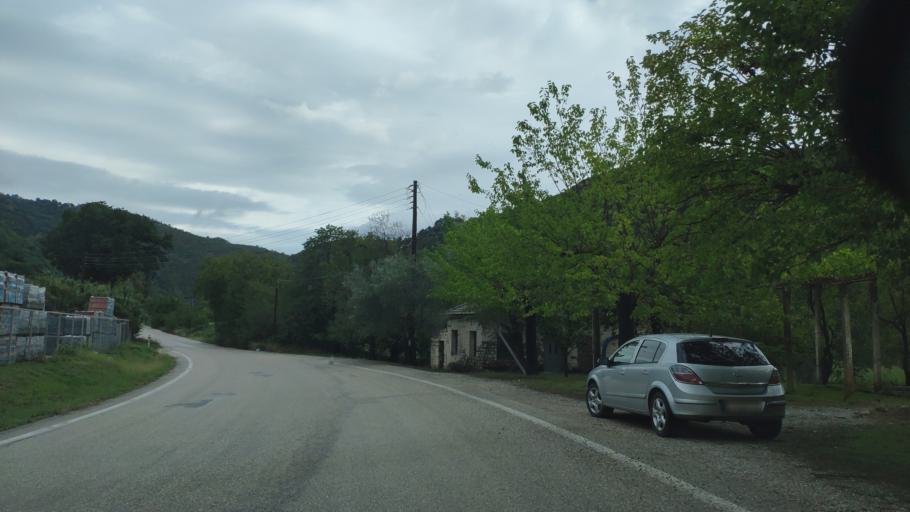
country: GR
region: West Greece
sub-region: Nomos Aitolias kai Akarnanias
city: Sardinia
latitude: 38.9150
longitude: 21.3571
